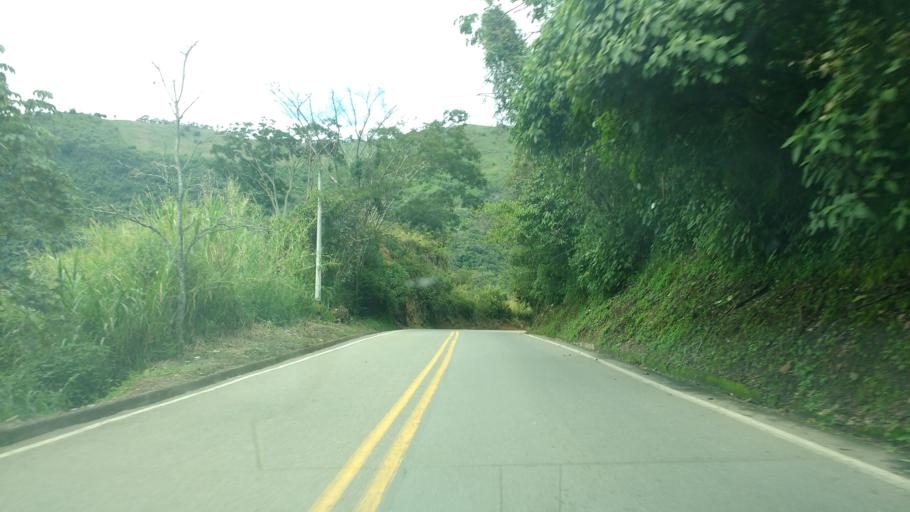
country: CO
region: Antioquia
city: Amaga
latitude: 6.0612
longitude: -75.7361
